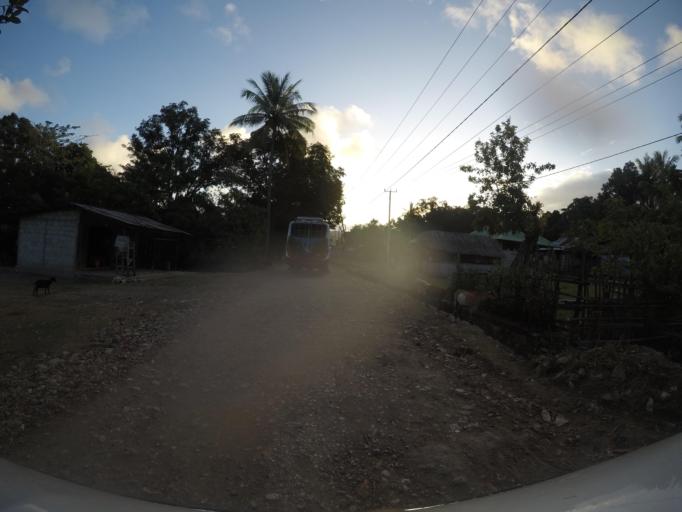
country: TL
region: Baucau
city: Venilale
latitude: -8.7487
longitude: 126.7049
